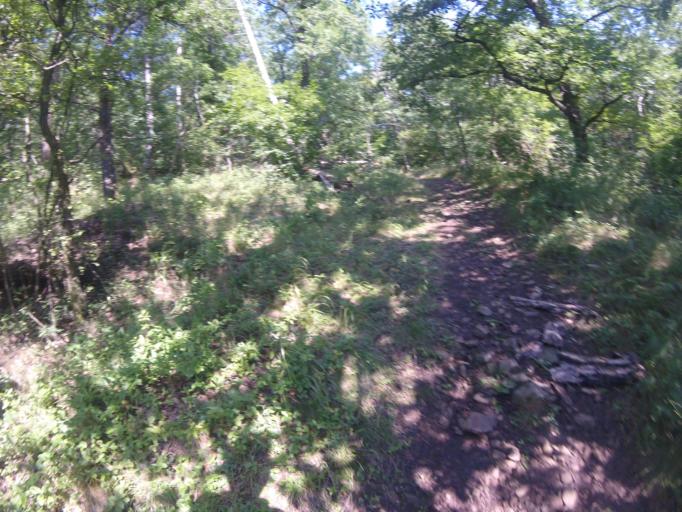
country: SK
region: Nitriansky
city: Sahy
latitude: 47.9901
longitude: 18.8934
